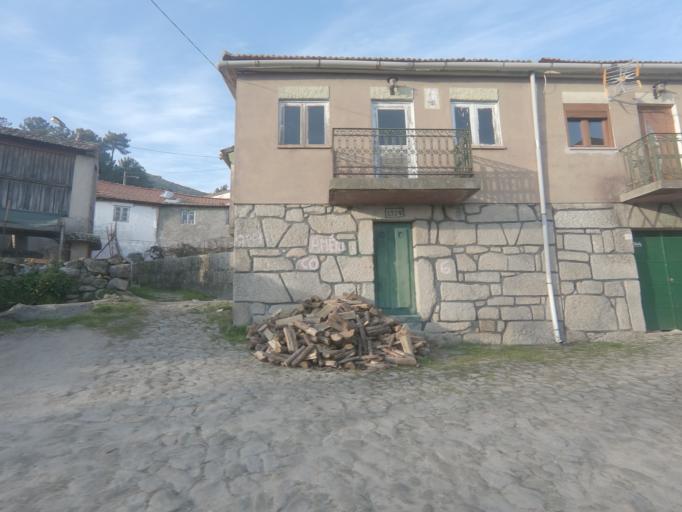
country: PT
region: Vila Real
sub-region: Vila Real
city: Vila Real
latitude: 41.3146
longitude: -7.7958
